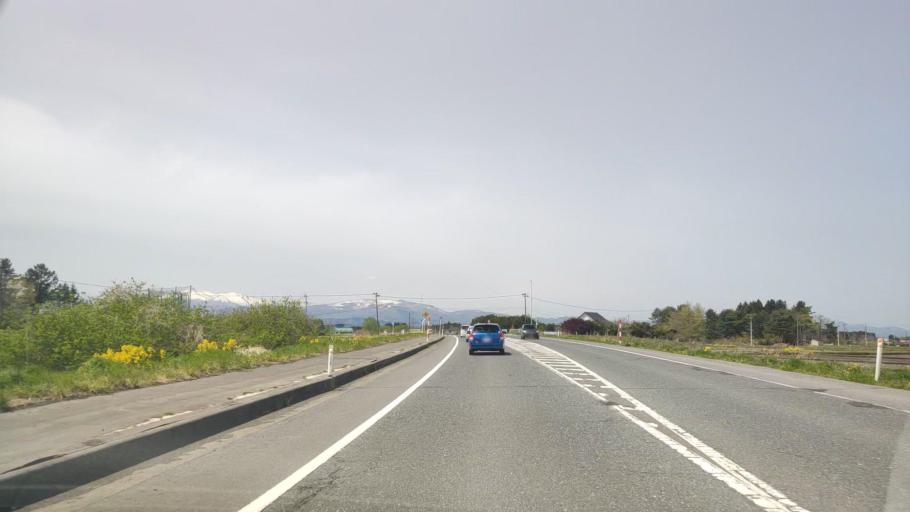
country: JP
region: Aomori
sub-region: Misawa Shi
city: Inuotose
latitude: 40.6379
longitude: 141.2398
